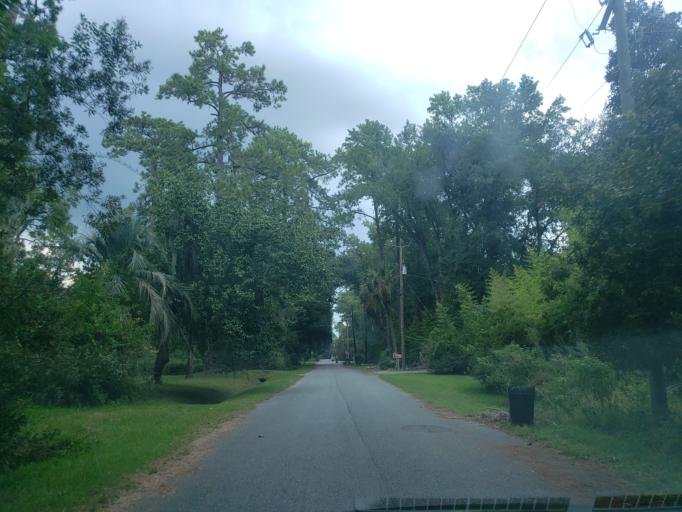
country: US
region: Georgia
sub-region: Chatham County
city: Isle of Hope
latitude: 31.9913
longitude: -81.0639
